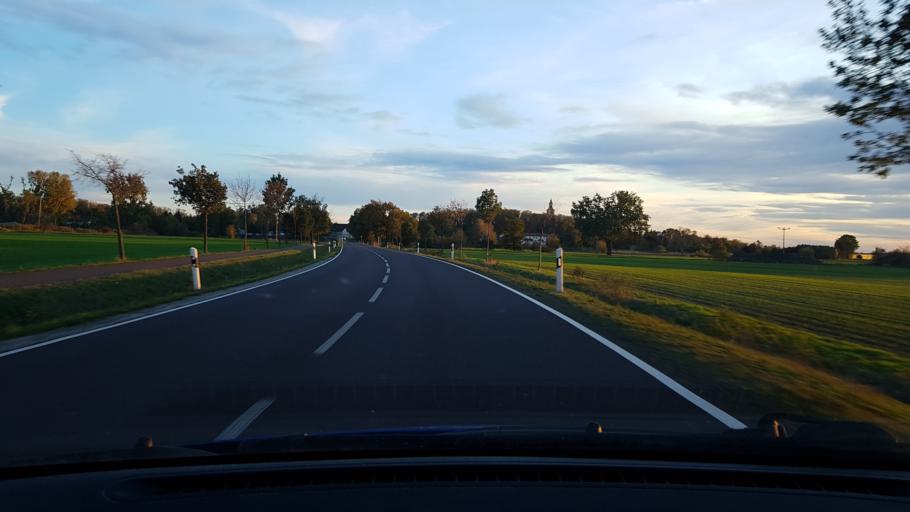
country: DE
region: Saxony-Anhalt
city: Wahlitz
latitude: 52.1236
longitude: 11.7626
